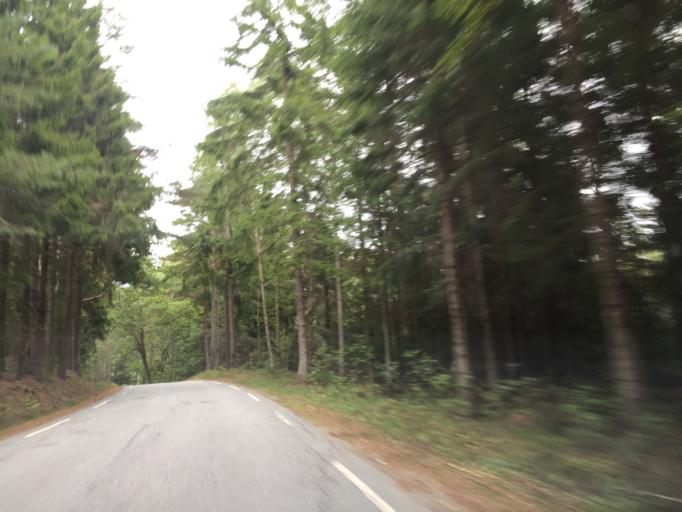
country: NO
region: Ostfold
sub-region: Hvaler
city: Skjaerhalden
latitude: 59.0573
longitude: 11.0599
